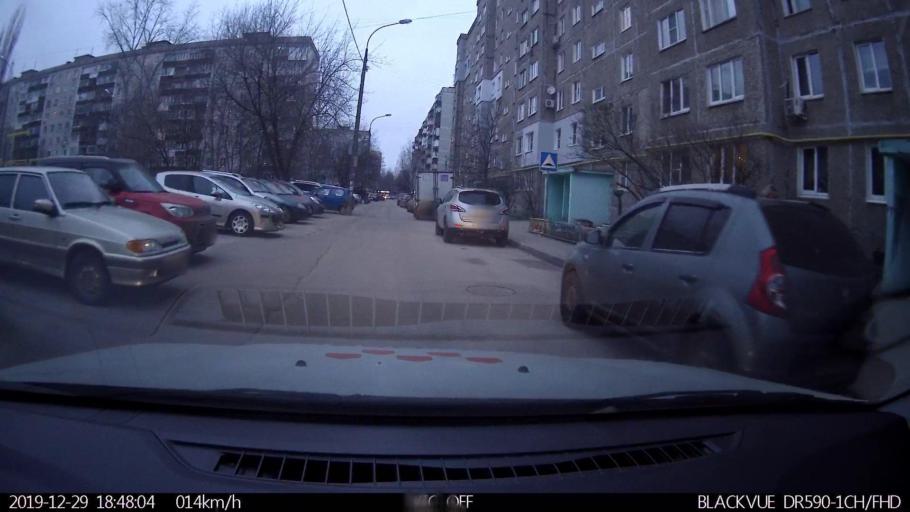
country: RU
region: Nizjnij Novgorod
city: Gorbatovka
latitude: 56.3418
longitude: 43.8407
